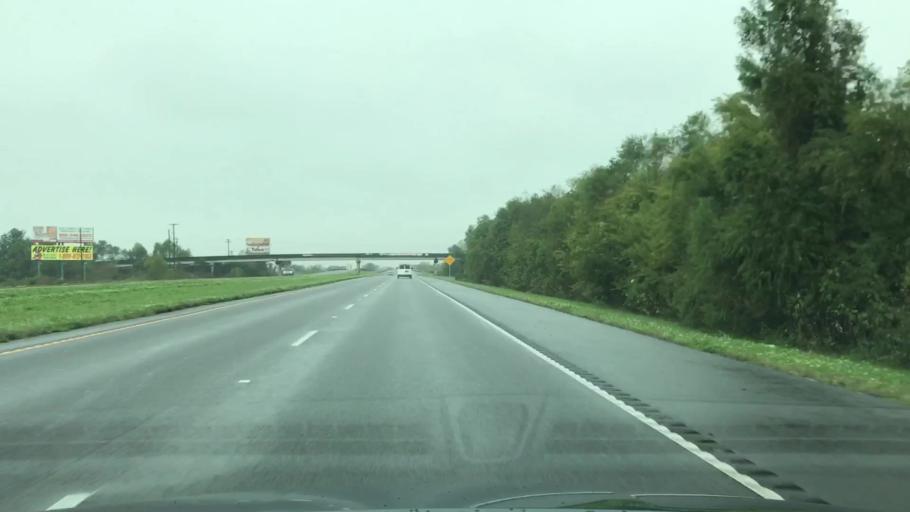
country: US
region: Louisiana
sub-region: Lafourche Parish
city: Raceland
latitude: 29.6903
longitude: -90.5995
